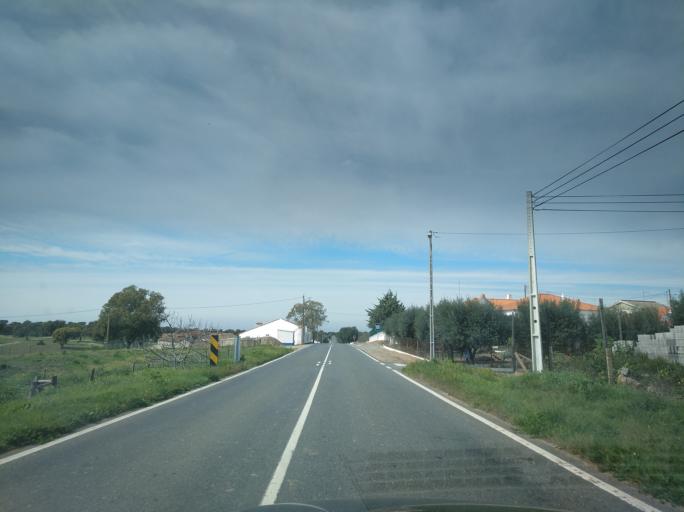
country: PT
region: Beja
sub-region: Mertola
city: Mertola
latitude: 37.7434
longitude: -7.7929
